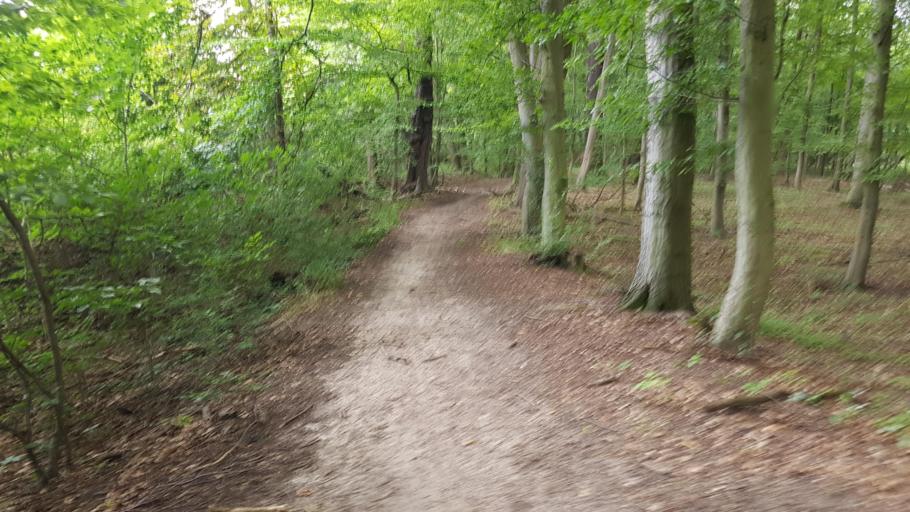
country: DE
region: Brandenburg
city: Sonnewalde
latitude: 51.6973
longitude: 13.6298
